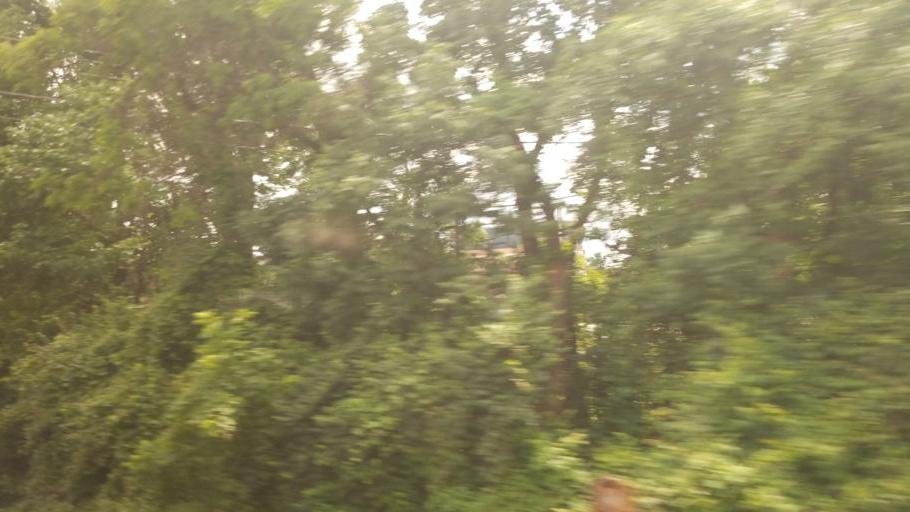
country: US
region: Maryland
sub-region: Montgomery County
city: Forest Glen
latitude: 39.0081
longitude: -77.0517
